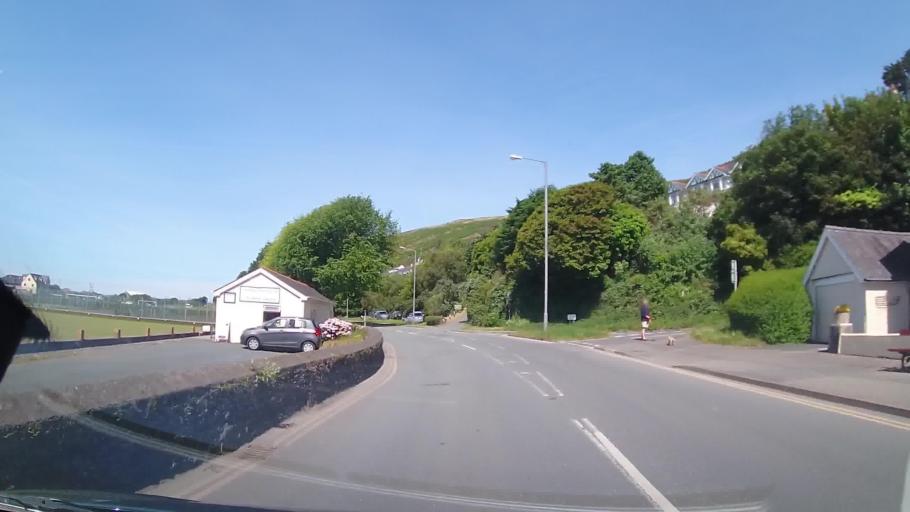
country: GB
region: Wales
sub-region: Gwynedd
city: Tywyn
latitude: 52.5450
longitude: -4.0533
